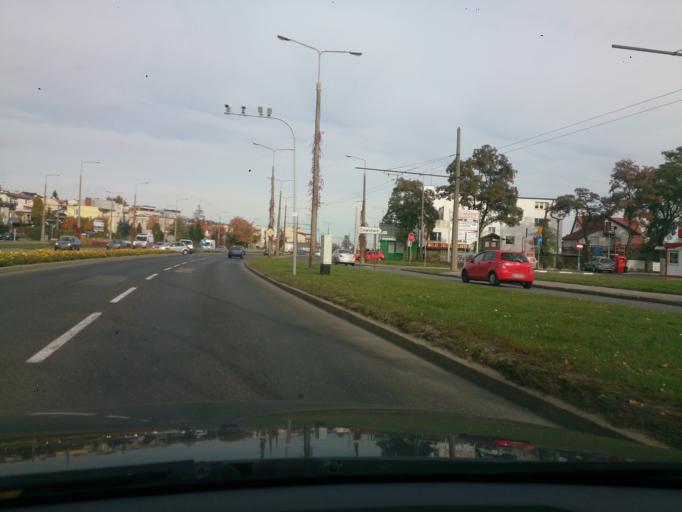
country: PL
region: Pomeranian Voivodeship
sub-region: Gdynia
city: Wielki Kack
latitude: 54.4745
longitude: 18.5154
